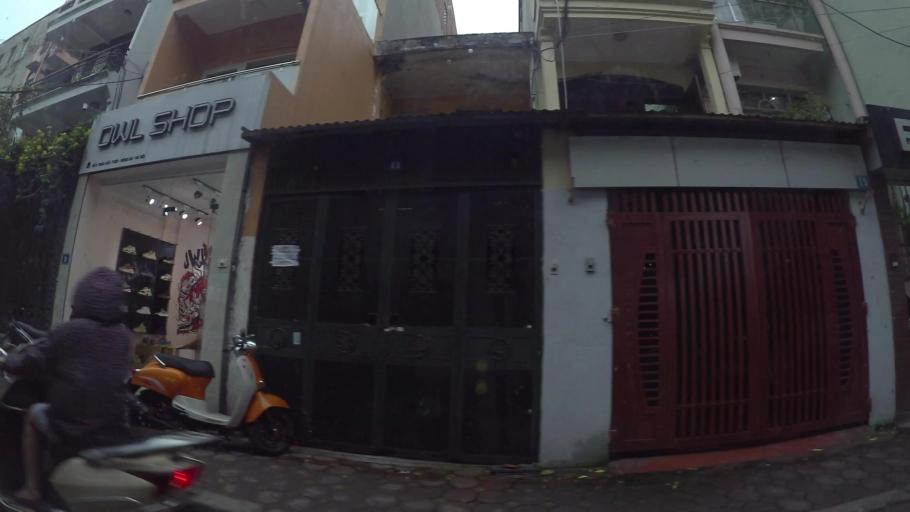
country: VN
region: Ha Noi
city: Dong Da
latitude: 21.0134
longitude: 105.8299
